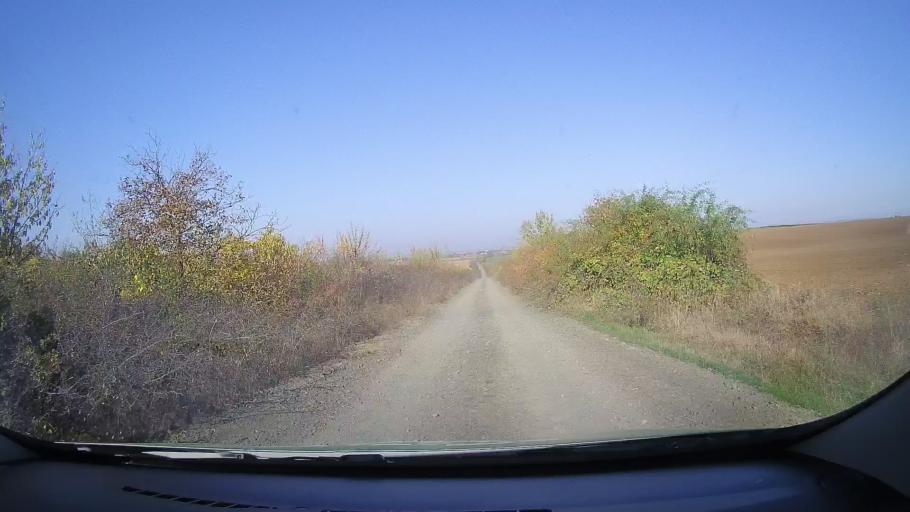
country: RO
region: Satu Mare
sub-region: Comuna Sauca
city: Sauca
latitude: 47.4781
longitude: 22.4738
